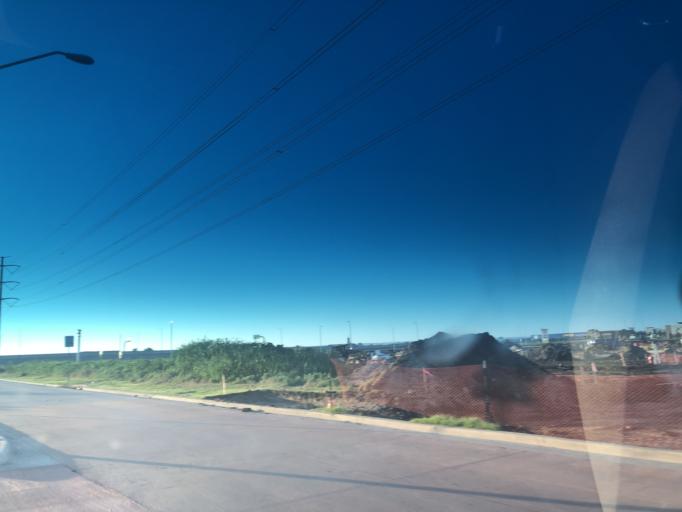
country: US
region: Texas
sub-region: Dallas County
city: Grand Prairie
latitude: 32.6986
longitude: -97.0280
